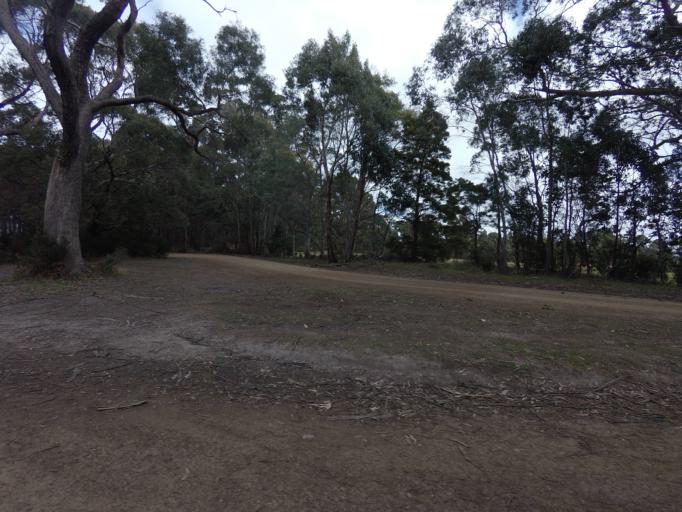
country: AU
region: Tasmania
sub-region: Huon Valley
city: Geeveston
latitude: -43.4373
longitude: 146.9887
